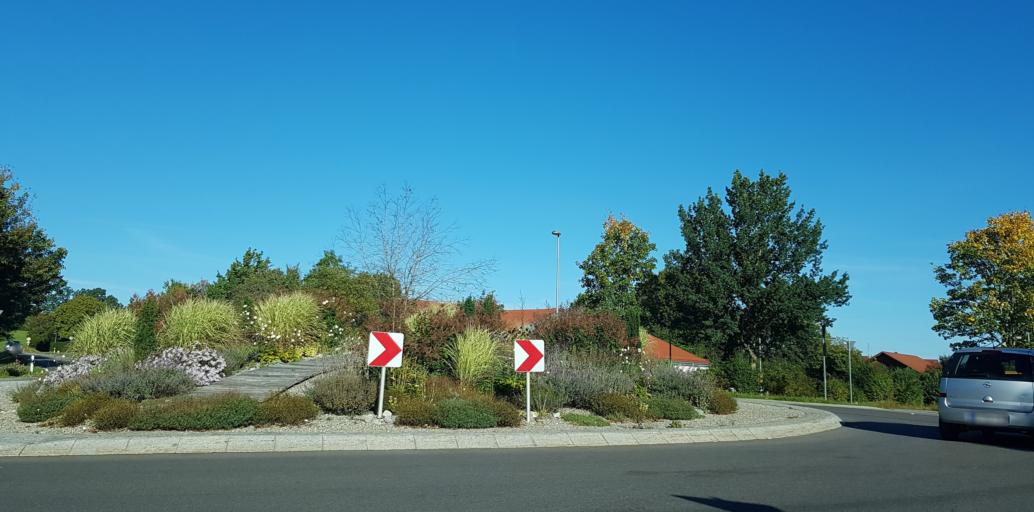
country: DE
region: Baden-Wuerttemberg
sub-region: Tuebingen Region
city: Bad Wurzach
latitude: 47.9028
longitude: 9.8945
